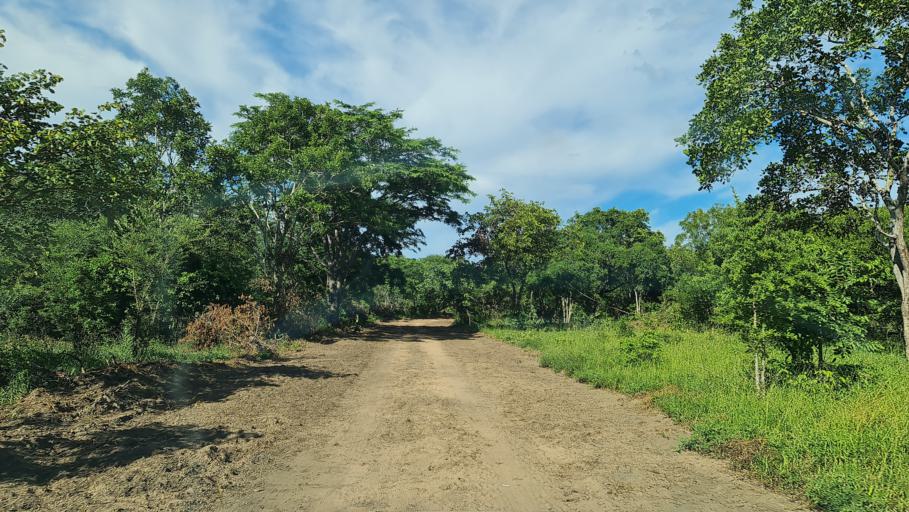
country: MZ
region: Nampula
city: Antonio Enes
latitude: -15.5106
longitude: 40.1338
